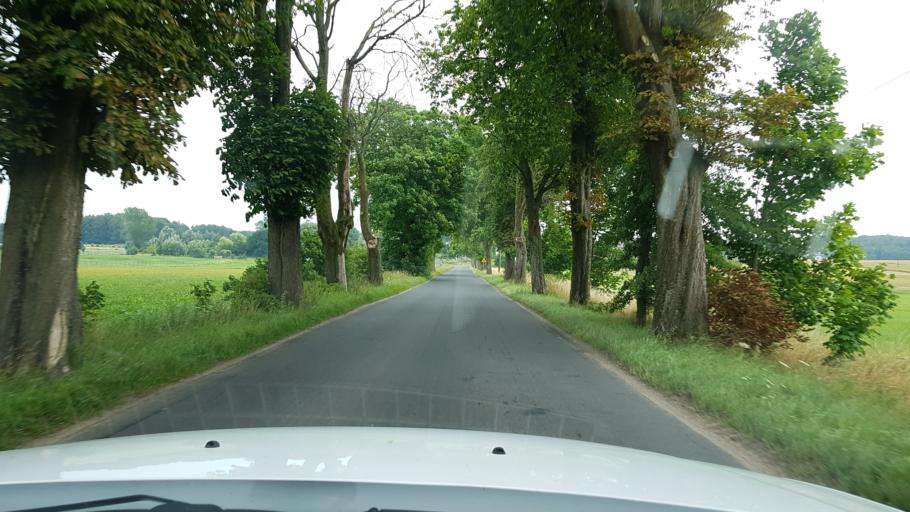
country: PL
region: West Pomeranian Voivodeship
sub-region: Powiat slawienski
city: Slawno
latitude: 54.4934
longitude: 16.5783
